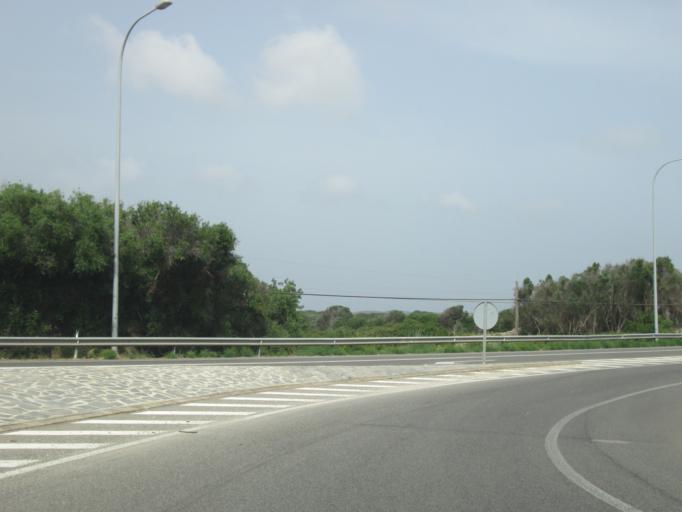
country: ES
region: Balearic Islands
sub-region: Illes Balears
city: Mao
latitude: 39.8930
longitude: 4.2278
